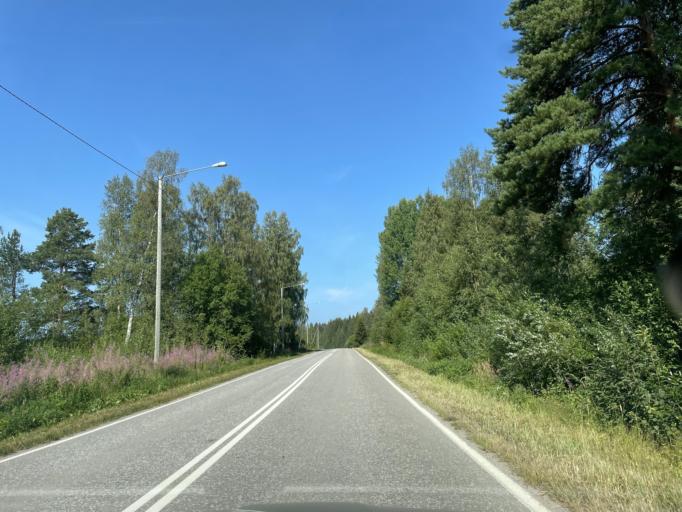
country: FI
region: Central Finland
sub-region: Saarijaervi-Viitasaari
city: Pihtipudas
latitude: 63.3595
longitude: 25.7492
